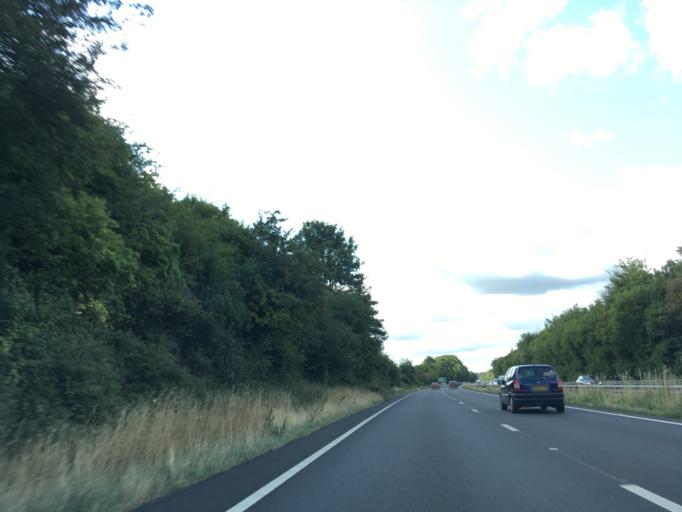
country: GB
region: England
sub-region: Hampshire
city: Highclere
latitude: 51.2902
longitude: -1.3380
